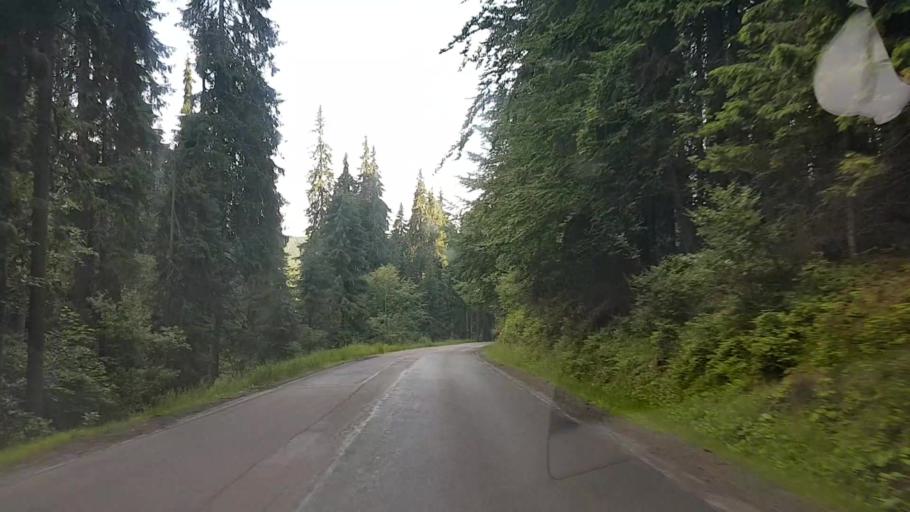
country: RO
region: Harghita
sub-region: Comuna Varsag
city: Varsag
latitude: 46.6489
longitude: 25.2886
